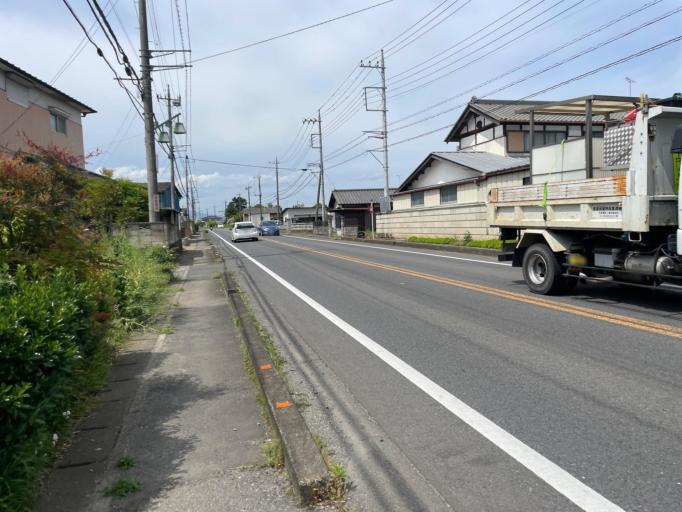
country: JP
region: Tochigi
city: Mibu
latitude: 36.4595
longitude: 139.7713
